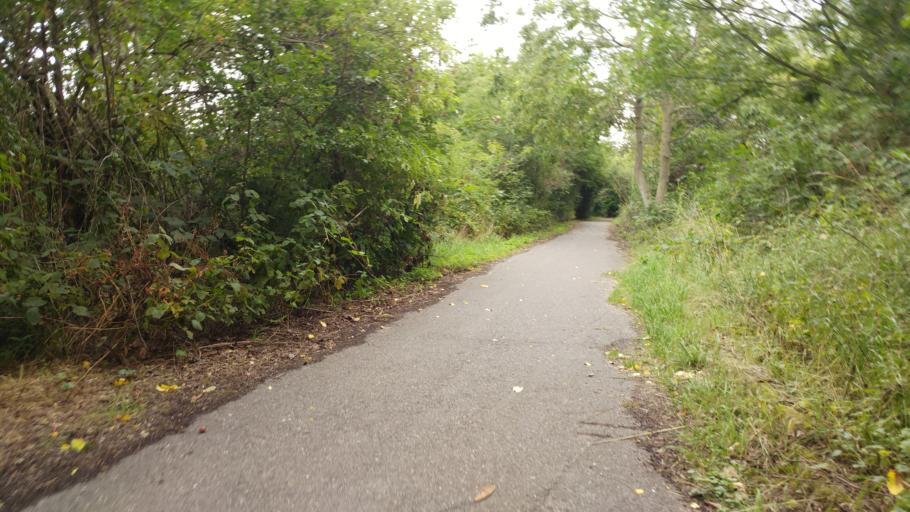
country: CZ
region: Central Bohemia
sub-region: Okres Praha-Zapad
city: Pruhonice
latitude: 50.0374
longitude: 14.5357
